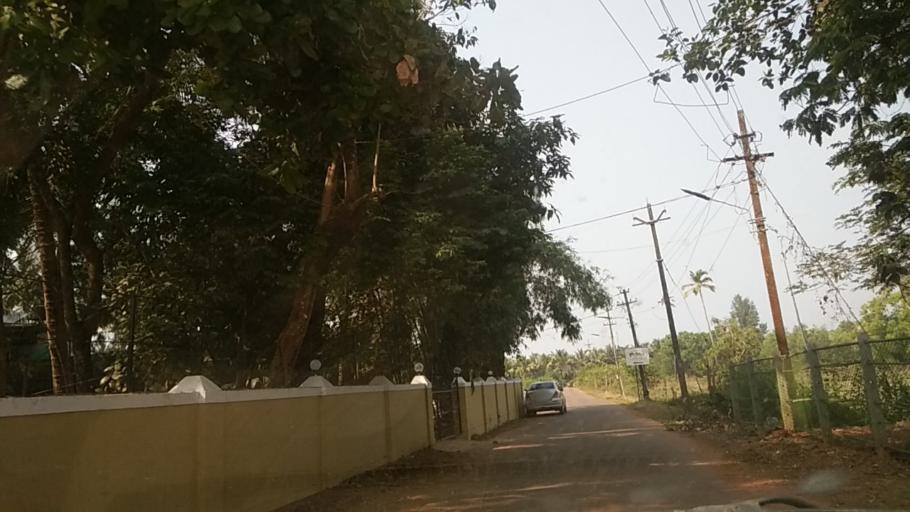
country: IN
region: Goa
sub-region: South Goa
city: Colva
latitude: 15.2880
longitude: 73.9116
